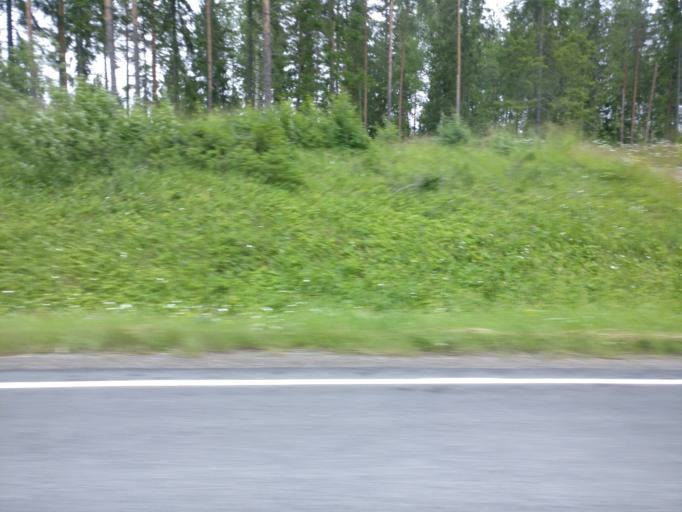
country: FI
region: Northern Savo
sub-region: Varkaus
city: Leppaevirta
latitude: 62.6103
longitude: 27.6233
